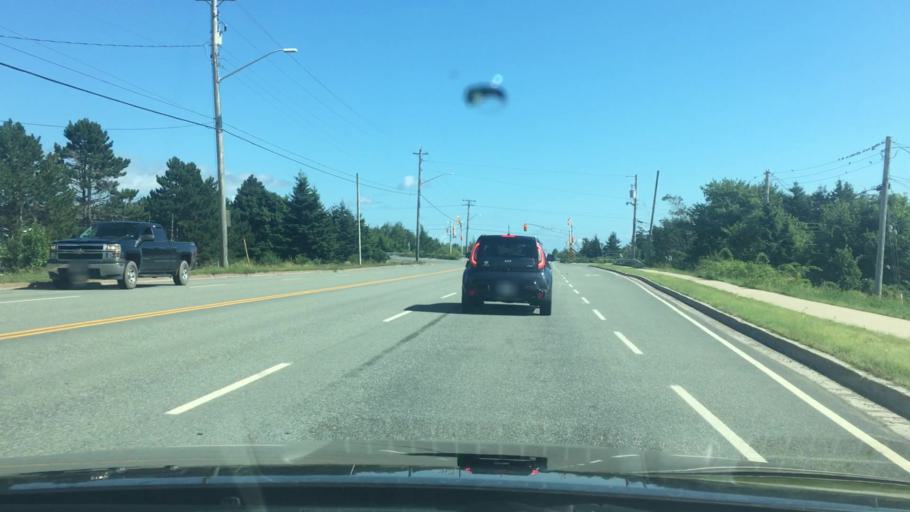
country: CA
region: Nova Scotia
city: Port Hawkesbury
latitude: 45.6128
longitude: -61.3465
